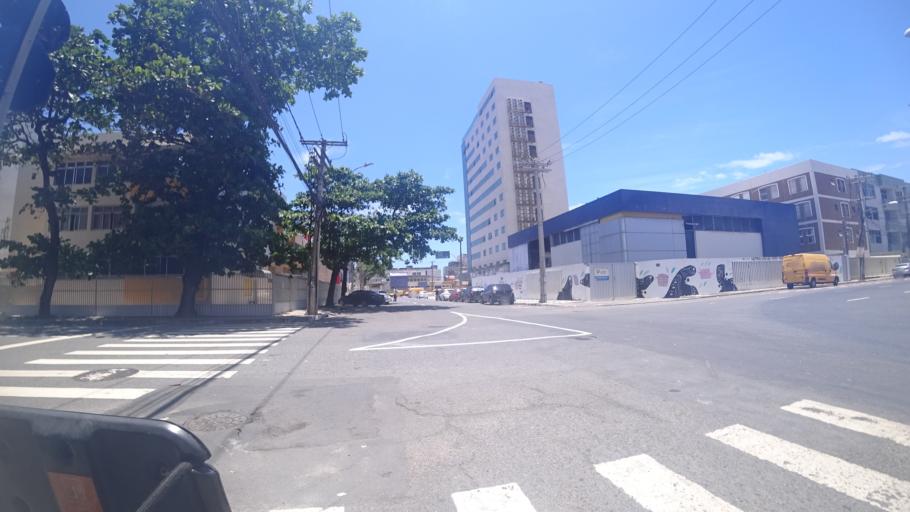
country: BR
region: Bahia
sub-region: Salvador
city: Salvador
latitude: -13.0125
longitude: -38.4699
